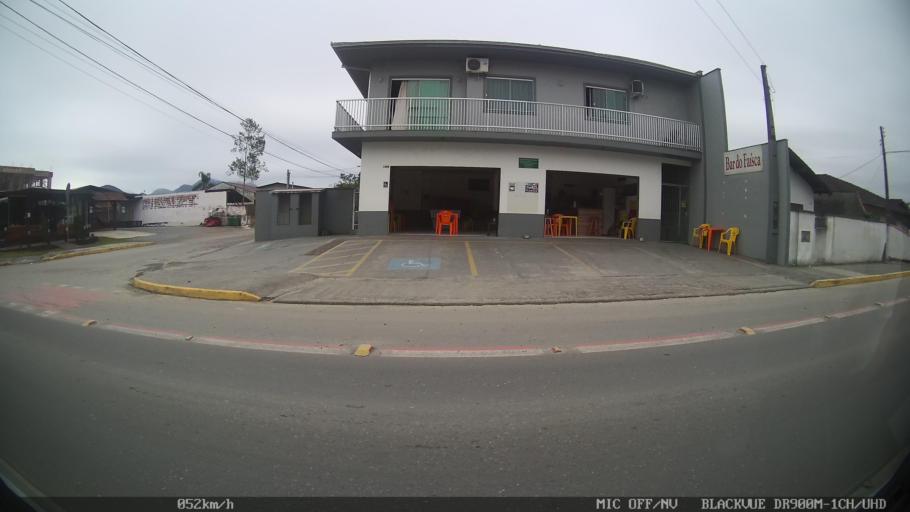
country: BR
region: Santa Catarina
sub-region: Joinville
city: Joinville
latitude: -26.2917
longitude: -48.9059
